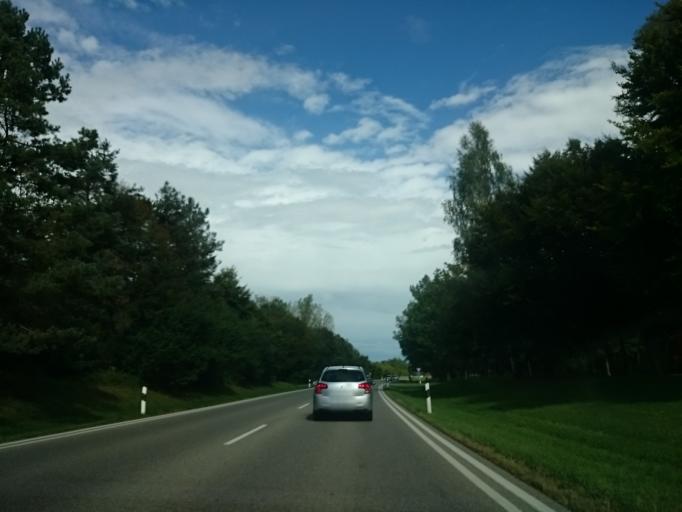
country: DE
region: Bavaria
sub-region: Swabia
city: Mauerstetten
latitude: 47.8778
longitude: 10.6450
